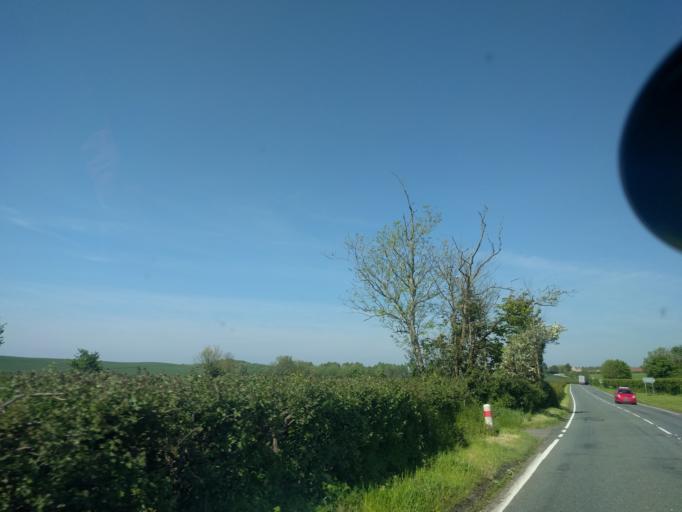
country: GB
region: England
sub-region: Somerset
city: Ilchester
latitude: 51.0268
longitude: -2.6962
